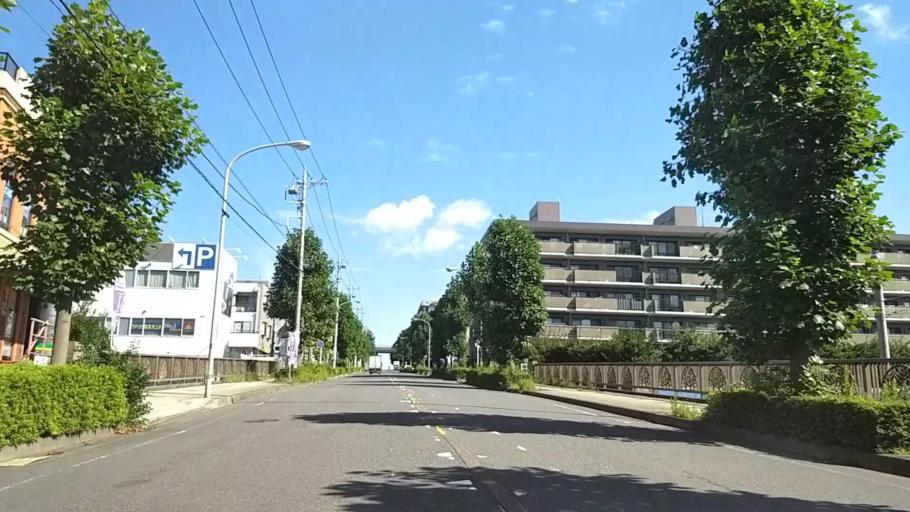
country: JP
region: Tokyo
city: Chofugaoka
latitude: 35.5629
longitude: 139.5532
